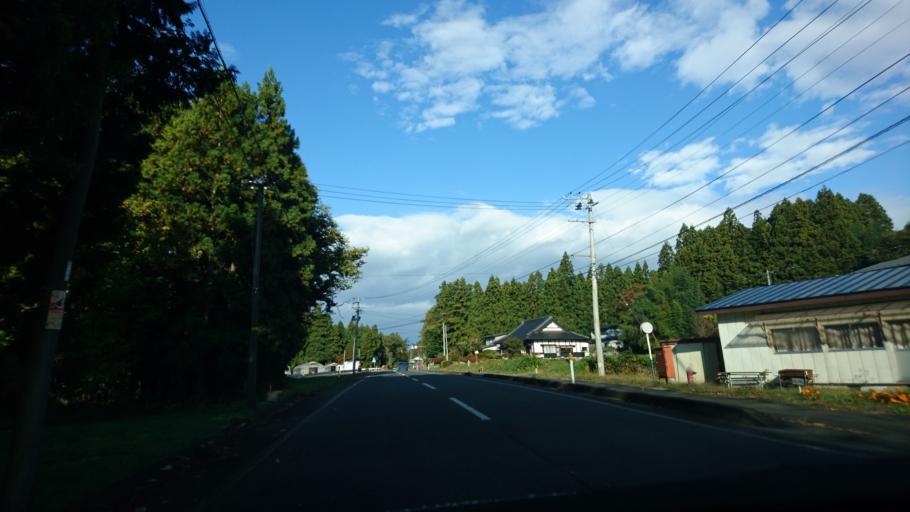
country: JP
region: Iwate
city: Mizusawa
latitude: 39.0351
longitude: 141.0743
